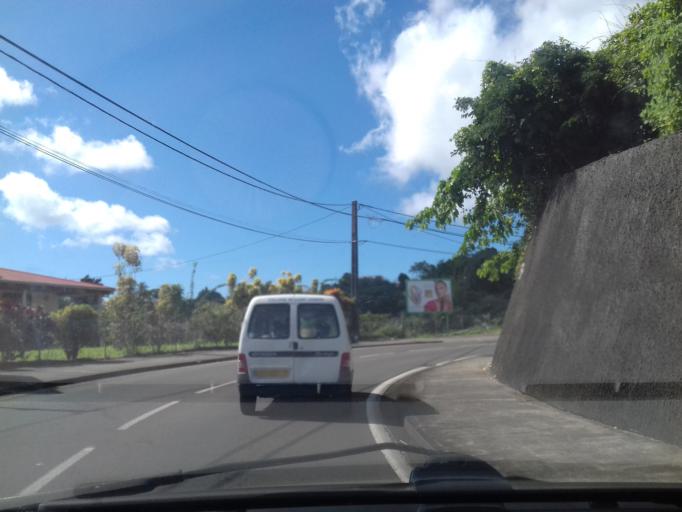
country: MQ
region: Martinique
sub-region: Martinique
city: Saint-Joseph
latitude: 14.6725
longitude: -61.0326
